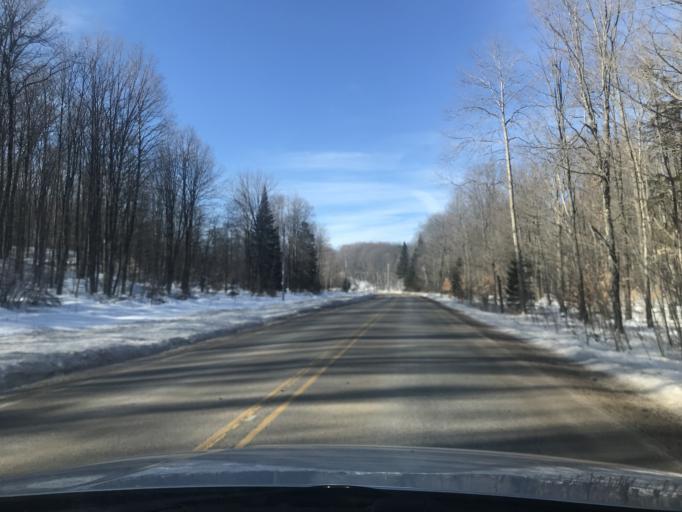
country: US
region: Michigan
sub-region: Dickinson County
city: Kingsford
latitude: 45.4194
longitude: -88.4130
